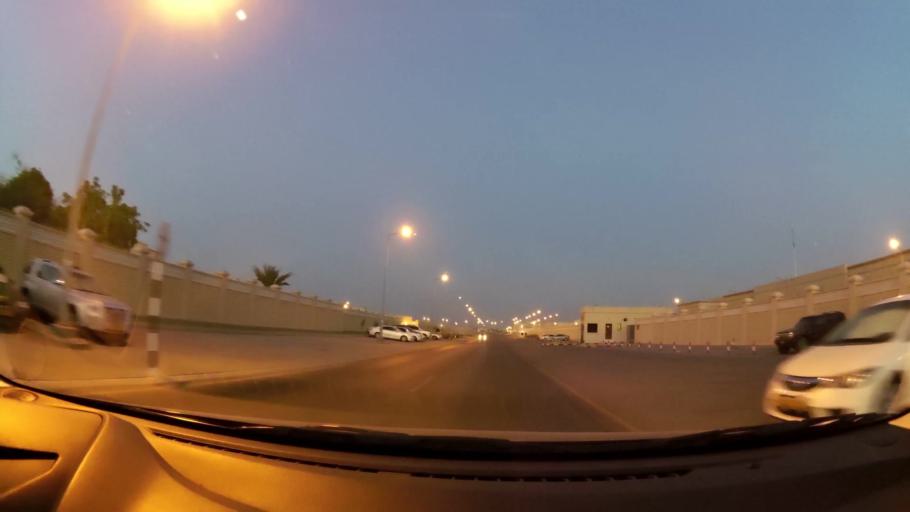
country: OM
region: Muhafazat Masqat
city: As Sib al Jadidah
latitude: 23.6644
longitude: 58.1846
